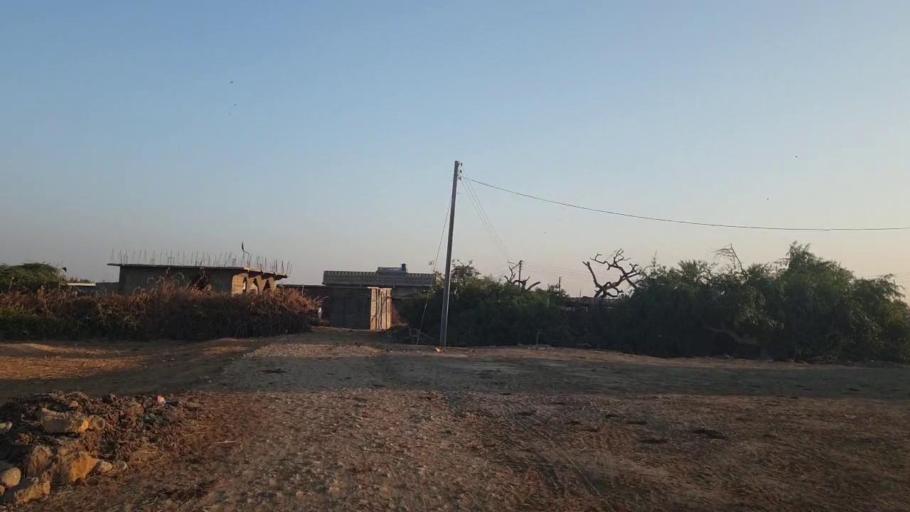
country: PK
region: Sindh
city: Mirpur Sakro
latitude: 24.4597
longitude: 67.5988
